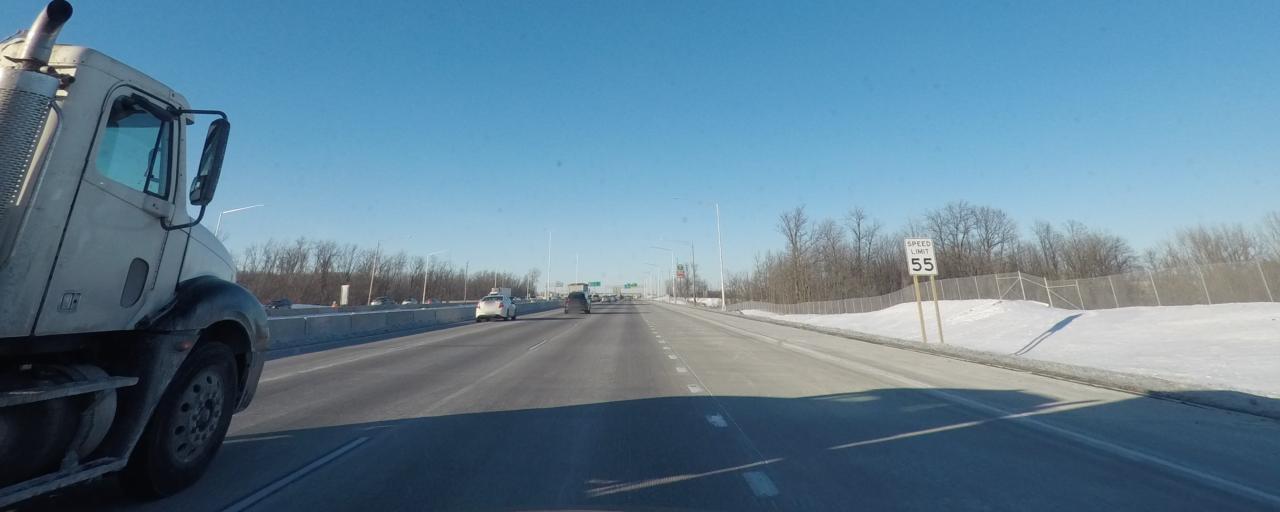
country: US
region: Wisconsin
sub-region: Milwaukee County
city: Greendale
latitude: 42.9077
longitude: -87.9358
